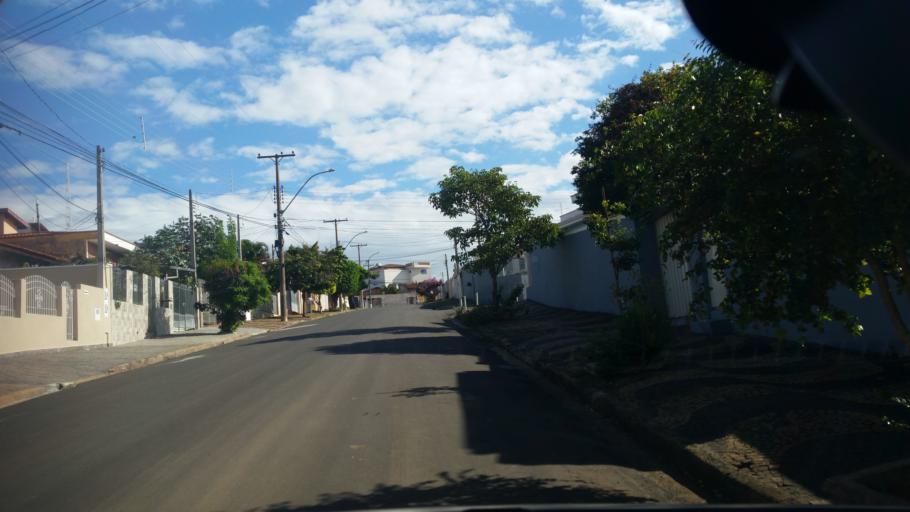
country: BR
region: Sao Paulo
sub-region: Campinas
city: Campinas
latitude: -22.8749
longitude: -47.0425
